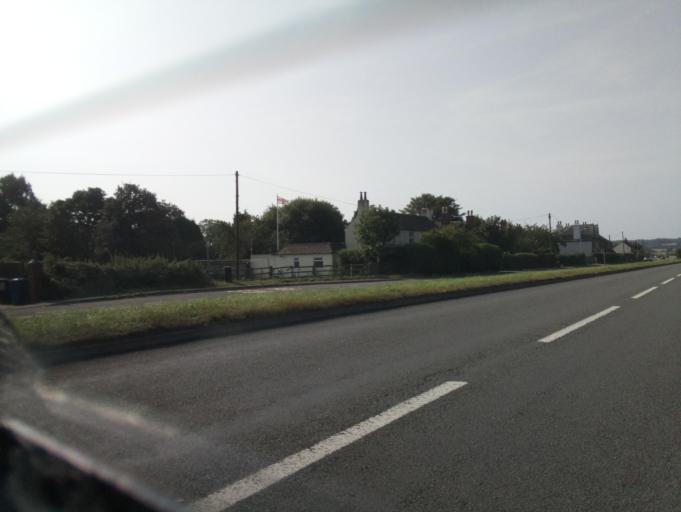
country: GB
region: England
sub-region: Staffordshire
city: Chasetown
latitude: 52.6545
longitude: -1.8847
